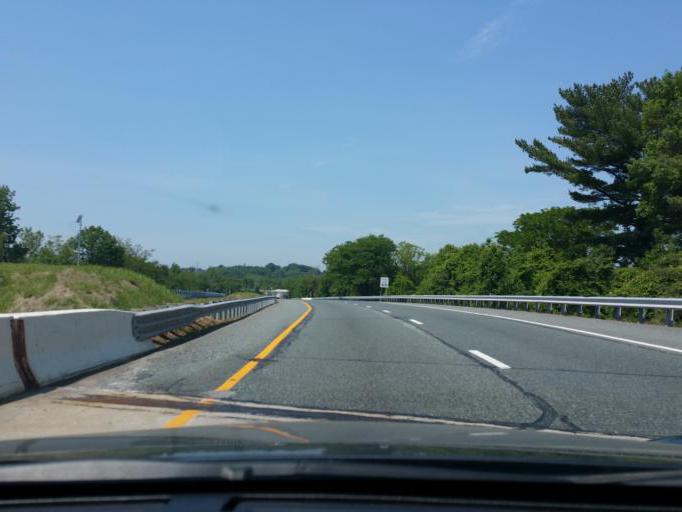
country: US
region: Maryland
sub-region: Howard County
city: Elkridge
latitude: 39.2217
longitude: -76.6939
